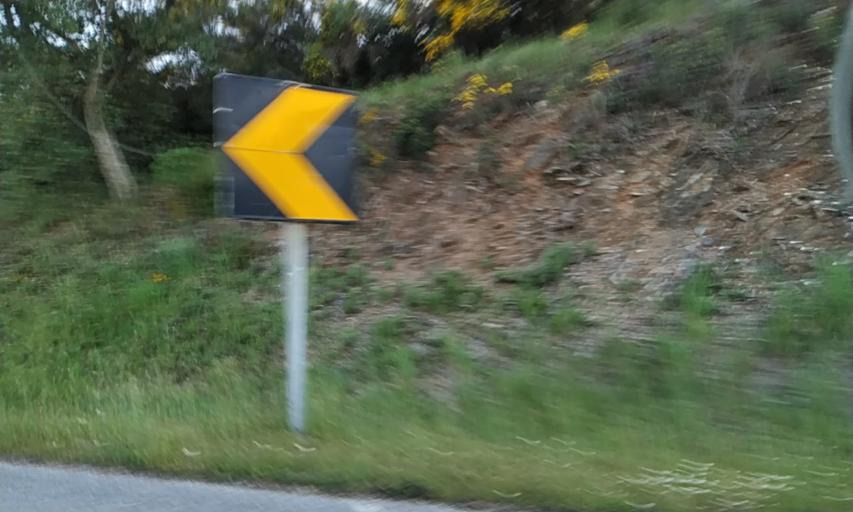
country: PT
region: Portalegre
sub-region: Portalegre
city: Sao Juliao
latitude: 39.3591
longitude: -7.3190
